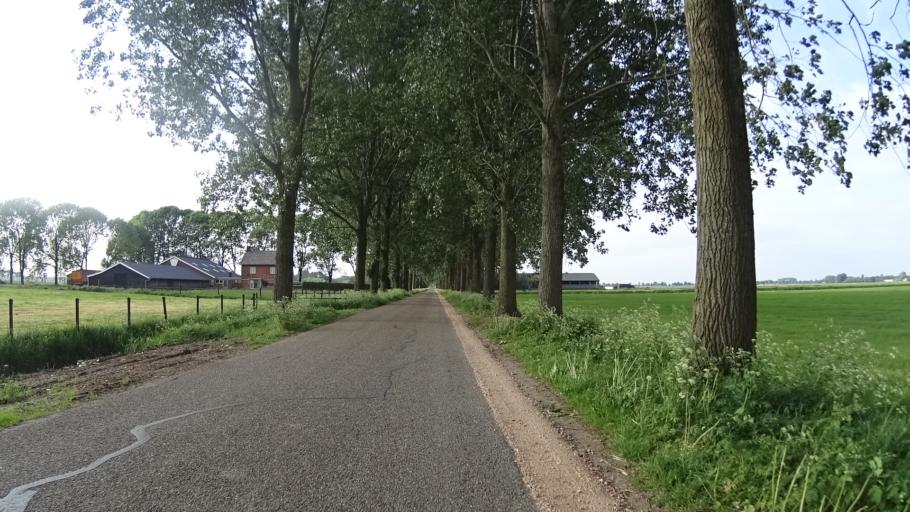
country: NL
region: North Brabant
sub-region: Gemeente Heusden
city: Heusden
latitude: 51.7174
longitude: 5.1612
